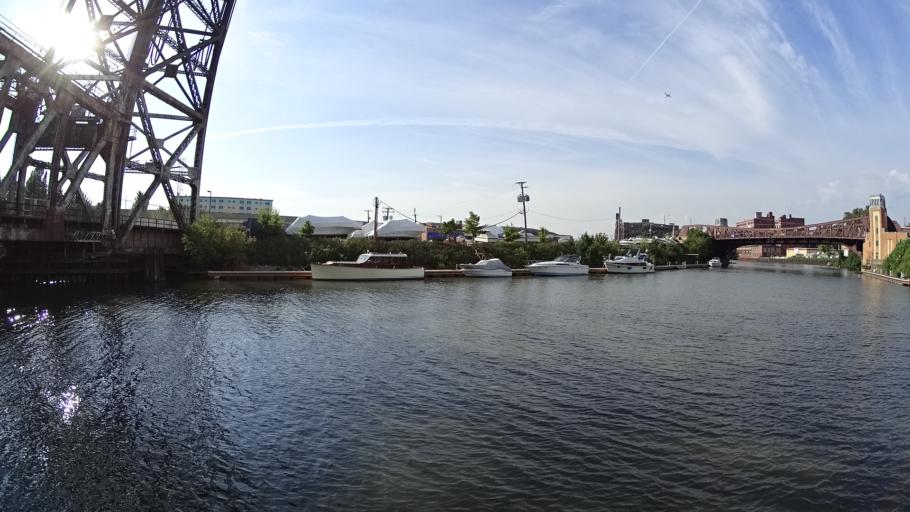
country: US
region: Illinois
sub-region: Cook County
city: Chicago
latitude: 41.8556
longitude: -87.6372
